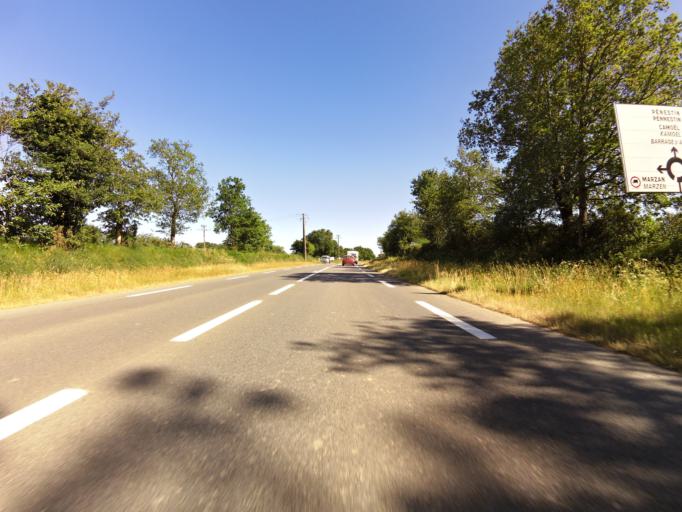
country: FR
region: Brittany
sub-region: Departement du Morbihan
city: Ferel
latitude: 47.5199
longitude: -2.3733
